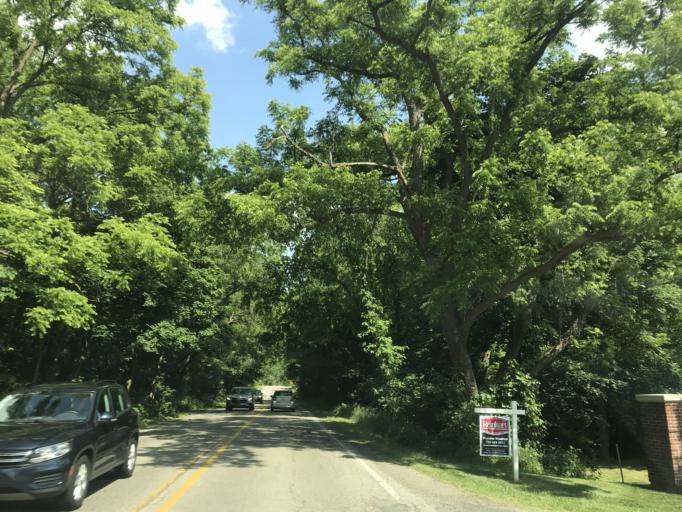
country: US
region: Michigan
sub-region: Washtenaw County
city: Ypsilanti
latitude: 42.2791
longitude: -83.6445
